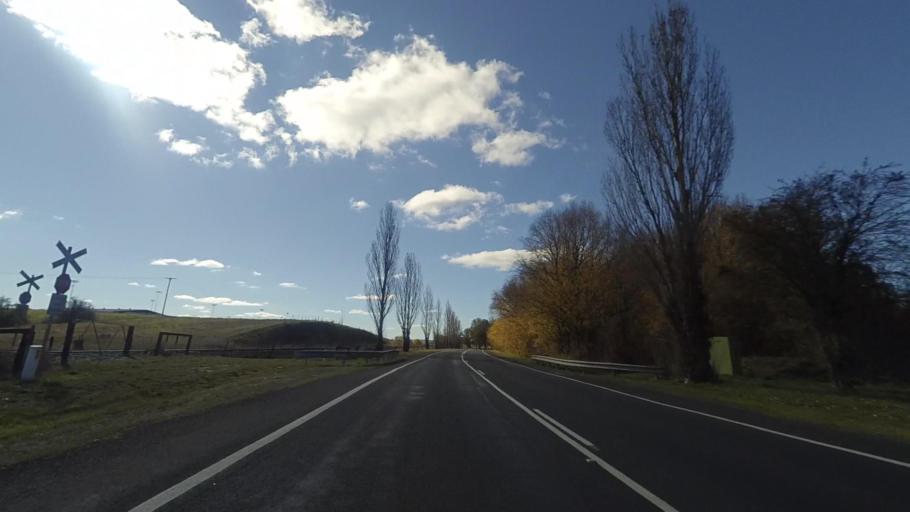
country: AU
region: New South Wales
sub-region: Bathurst Regional
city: Bathurst
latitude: -33.4548
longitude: 149.5761
